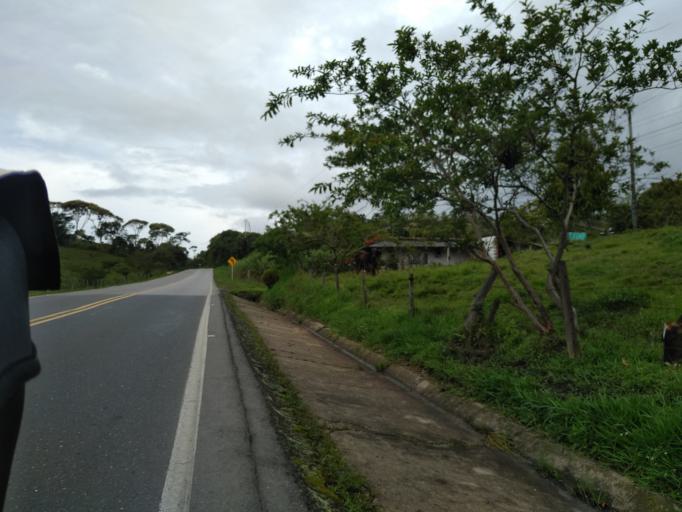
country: CO
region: Santander
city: Suaita
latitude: 6.1368
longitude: -73.3579
